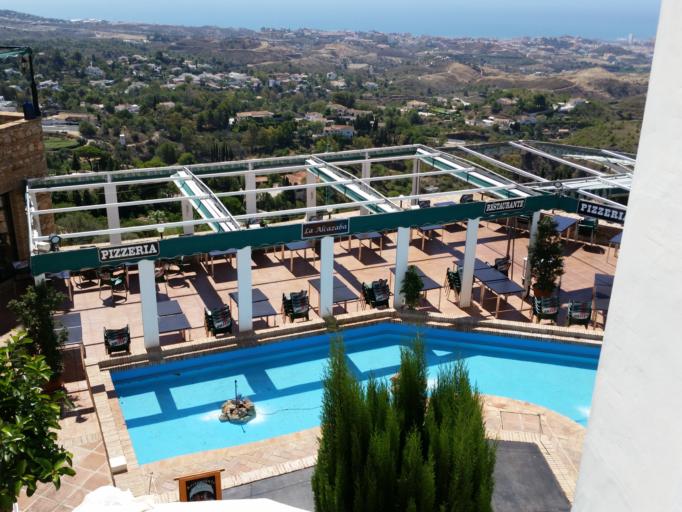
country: ES
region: Andalusia
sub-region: Provincia de Malaga
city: Mijas
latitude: 36.5944
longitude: -4.6382
